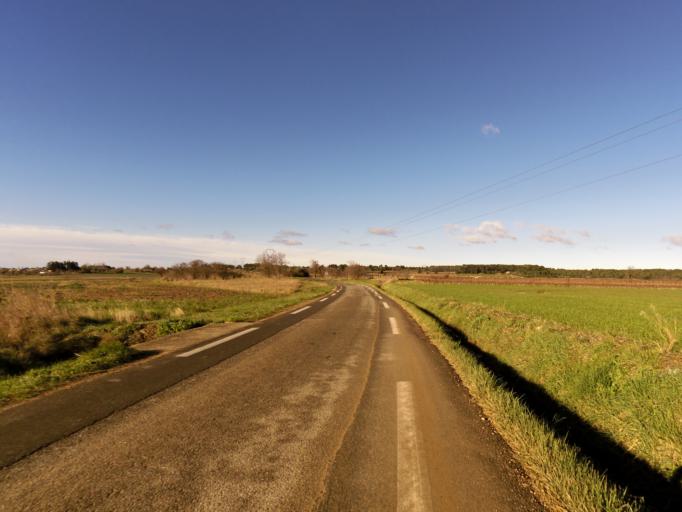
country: FR
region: Languedoc-Roussillon
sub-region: Departement du Gard
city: Aigues-Vives
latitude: 43.7495
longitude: 4.1872
